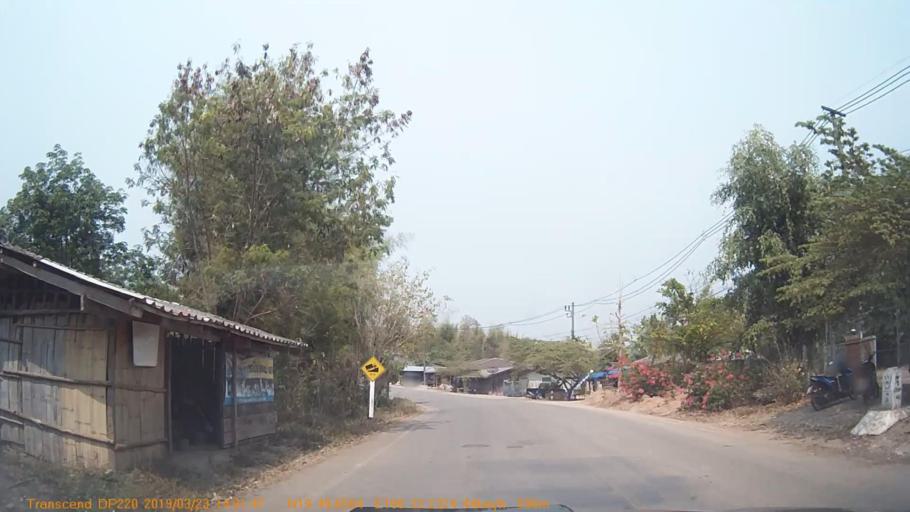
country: TH
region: Chiang Rai
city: Khun Tan
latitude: 19.8280
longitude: 100.3709
